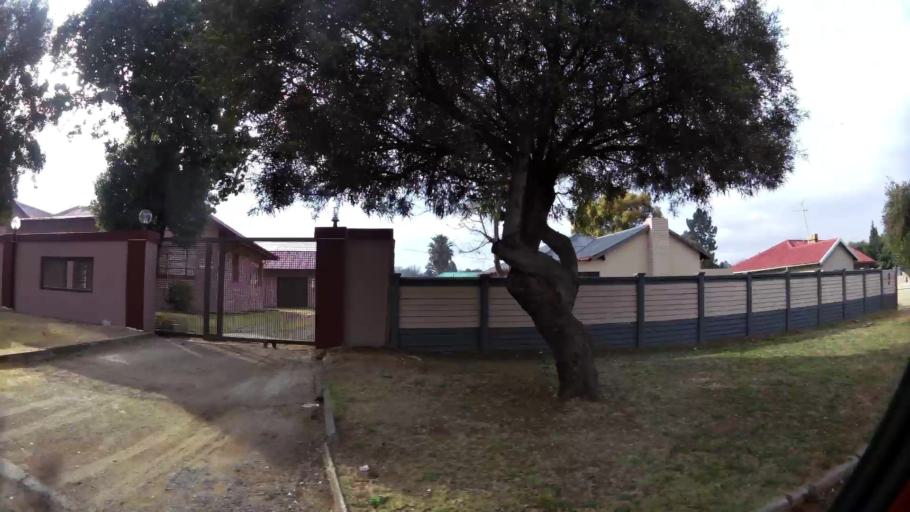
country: ZA
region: Gauteng
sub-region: Sedibeng District Municipality
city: Vanderbijlpark
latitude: -26.7033
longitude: 27.8182
